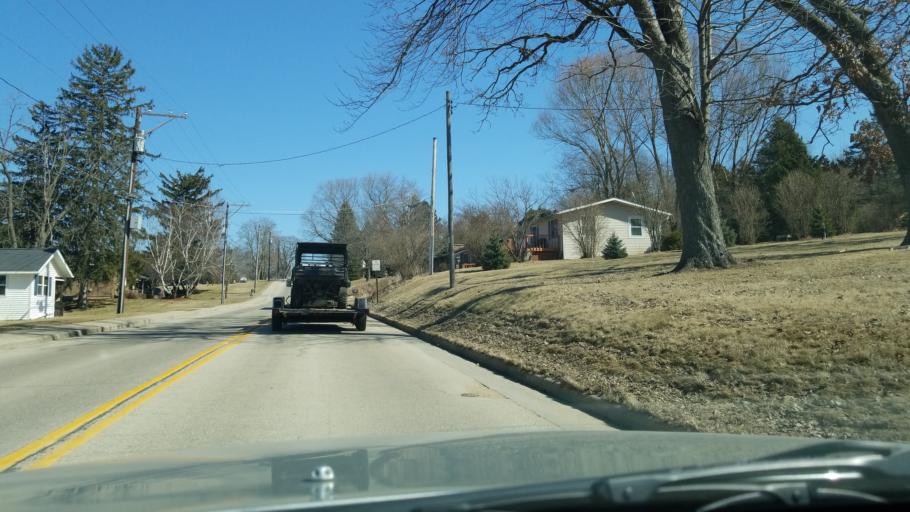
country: US
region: Wisconsin
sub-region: Iowa County
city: Mineral Point
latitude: 42.8605
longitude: -90.1945
